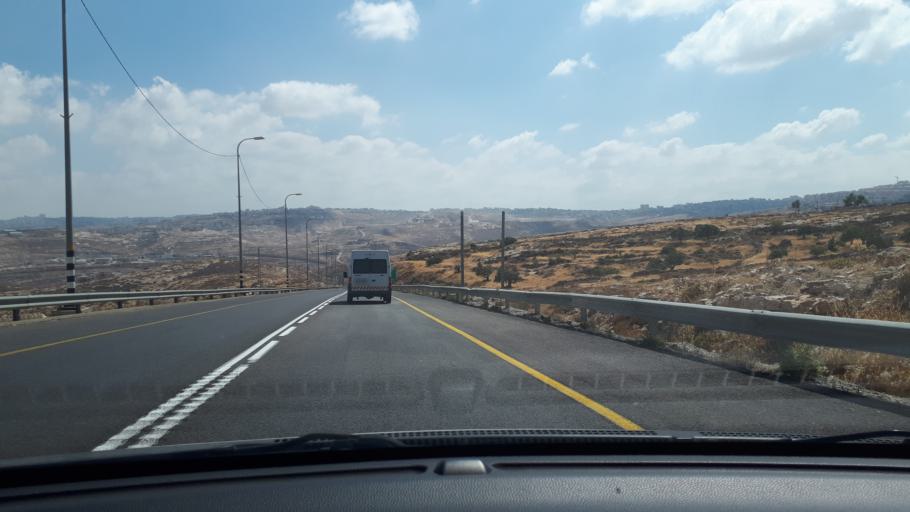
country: PS
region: West Bank
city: Mikhmas
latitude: 31.8842
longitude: 35.2736
